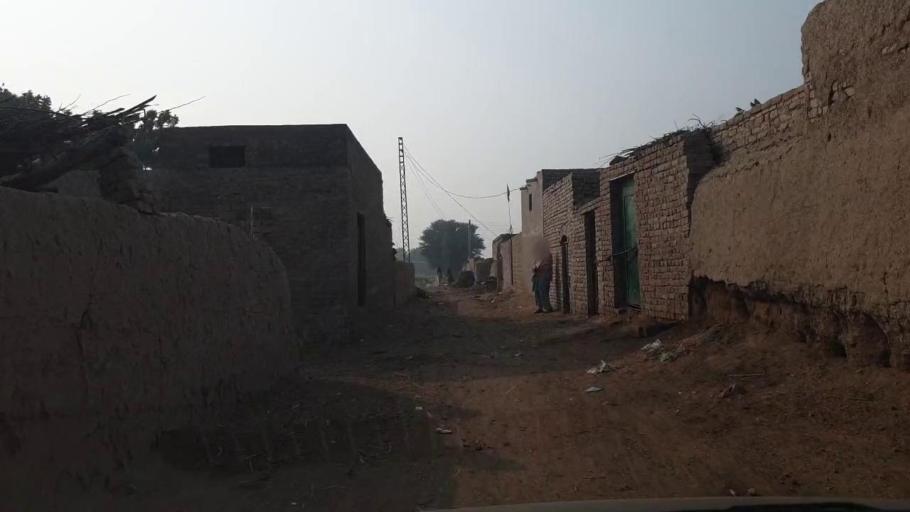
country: PK
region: Sindh
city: Hala
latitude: 25.8717
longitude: 68.3932
